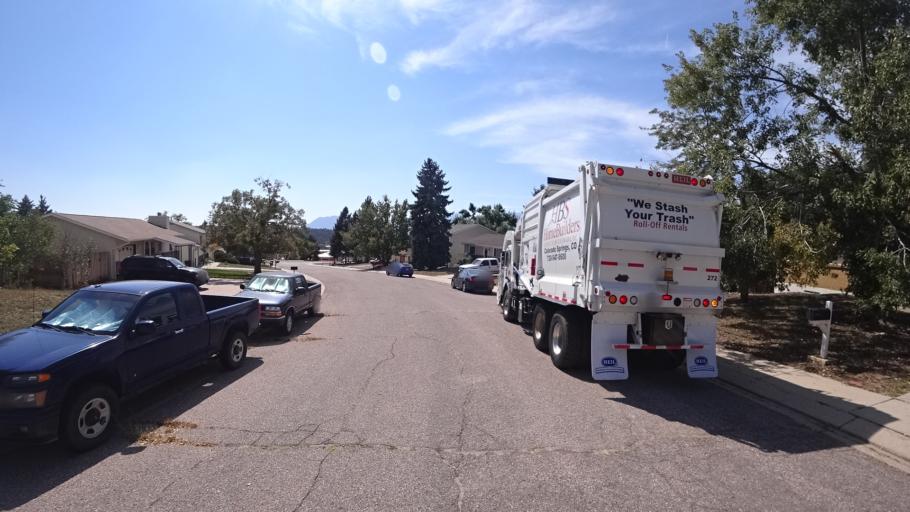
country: US
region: Colorado
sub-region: El Paso County
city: Colorado Springs
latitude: 38.9074
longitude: -104.7755
